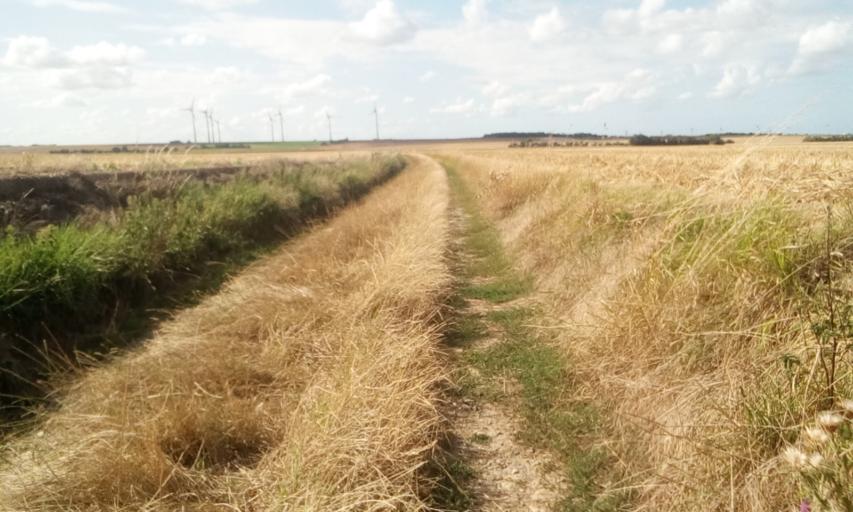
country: FR
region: Lower Normandy
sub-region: Departement du Calvados
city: Saint-Sylvain
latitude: 49.0784
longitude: -0.2363
